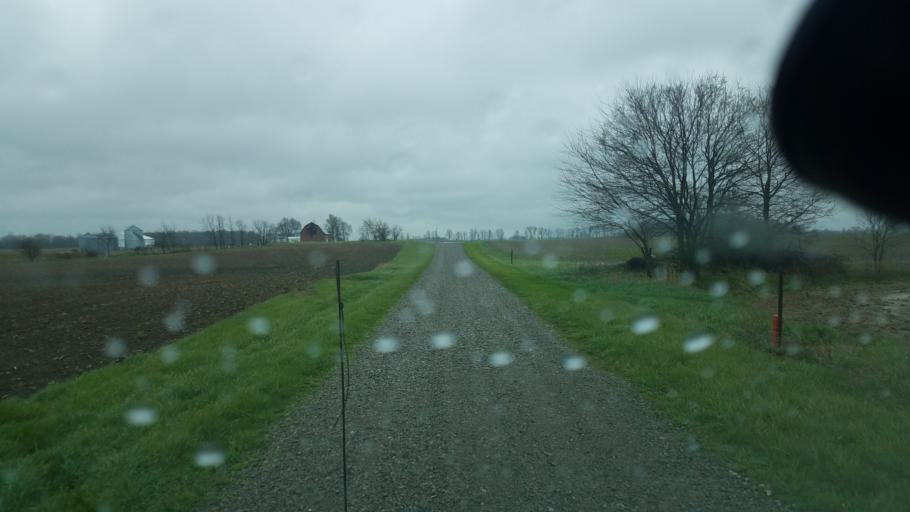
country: US
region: Ohio
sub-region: Union County
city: Richwood
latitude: 40.5181
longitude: -83.3603
